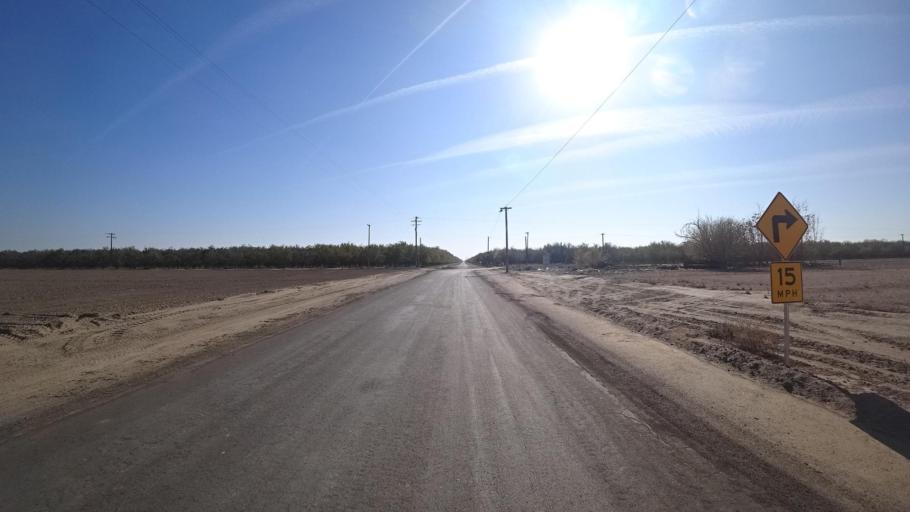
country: US
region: California
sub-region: Kern County
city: Wasco
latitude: 35.6605
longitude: -119.3840
